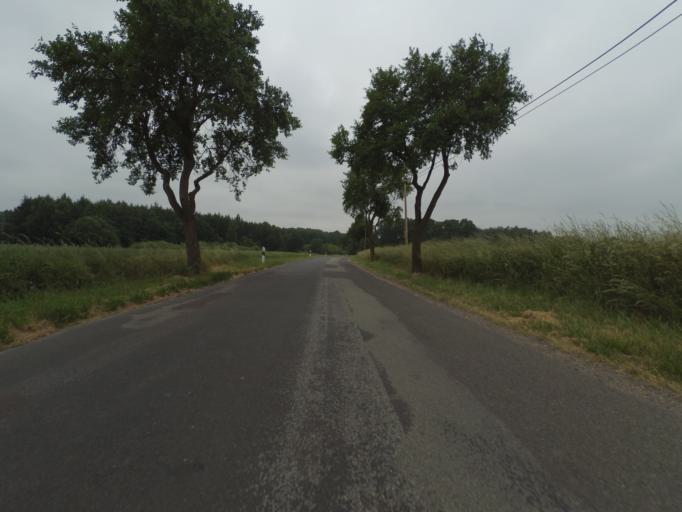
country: DE
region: Mecklenburg-Vorpommern
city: Plau am See
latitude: 53.4975
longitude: 12.1648
